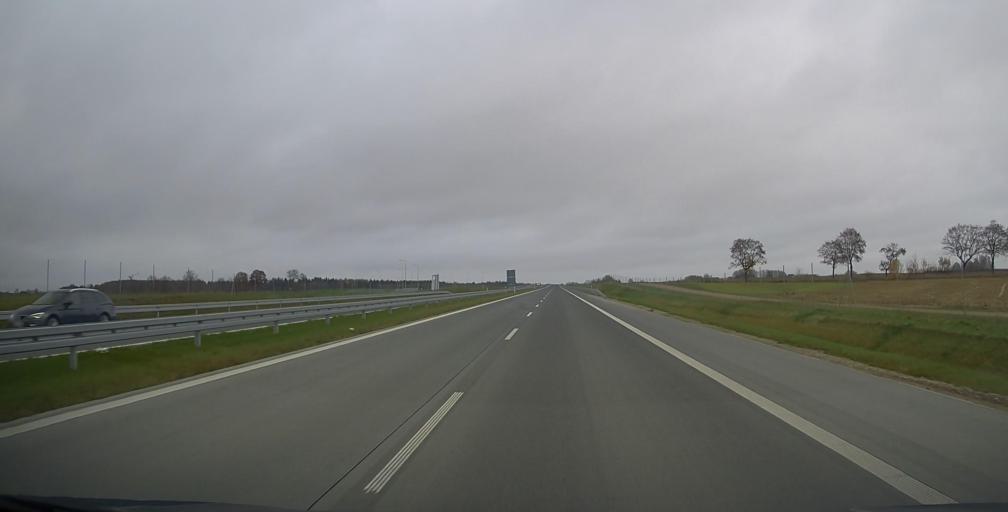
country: PL
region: Podlasie
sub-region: Powiat grajewski
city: Rajgrod
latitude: 53.8823
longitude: 22.6675
